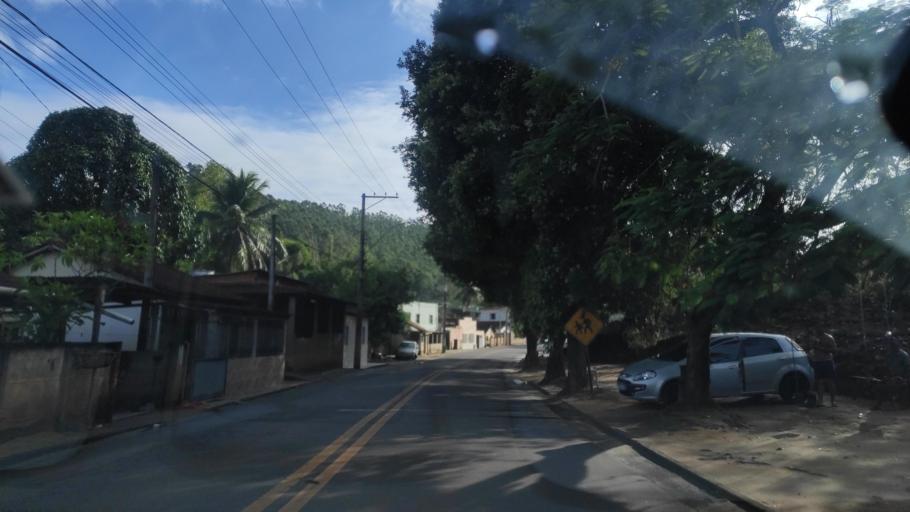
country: BR
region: Espirito Santo
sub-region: Nova Venecia
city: Nova Venecia
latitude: -18.7133
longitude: -40.3855
